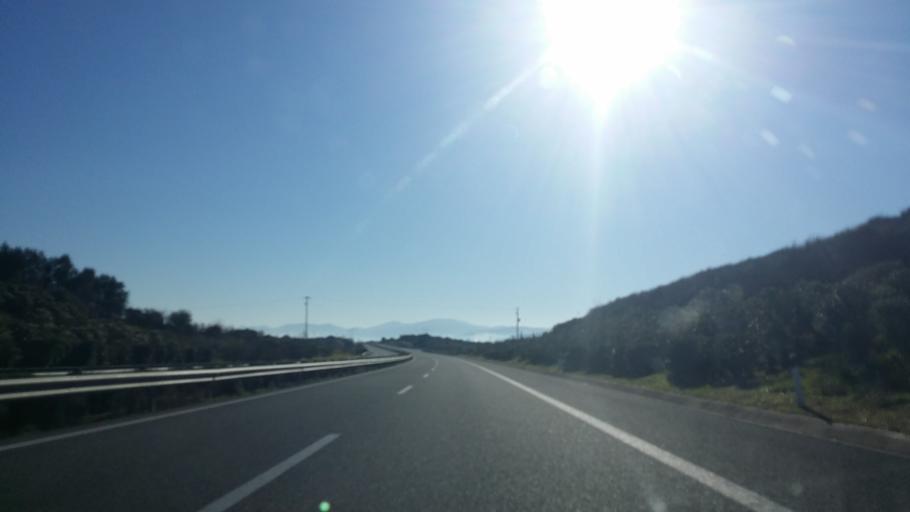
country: GR
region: West Greece
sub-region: Nomos Aitolias kai Akarnanias
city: Fitiai
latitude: 38.6767
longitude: 21.2220
